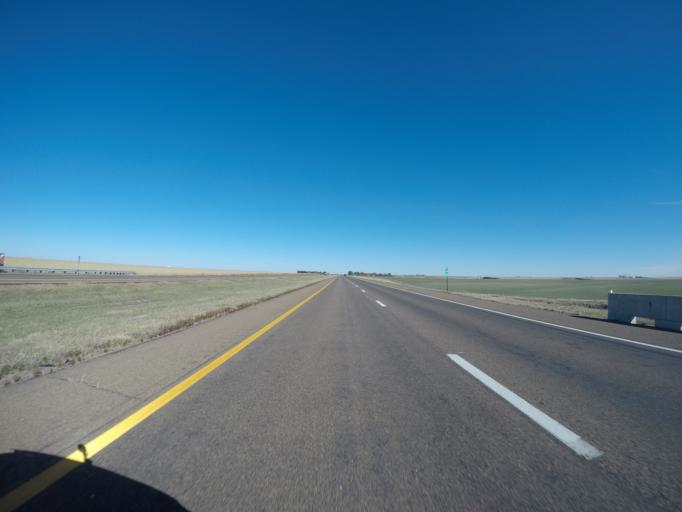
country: US
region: Kansas
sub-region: Thomas County
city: Colby
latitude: 39.3656
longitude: -101.1663
